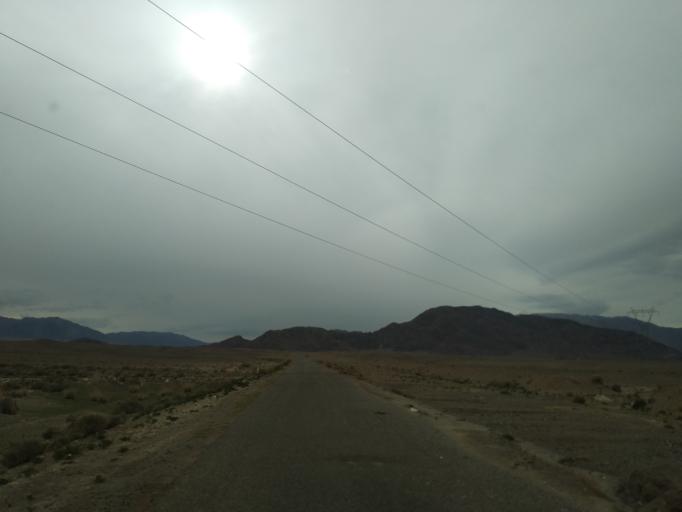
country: KG
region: Ysyk-Koel
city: Balykchy
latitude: 42.3202
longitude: 76.1819
